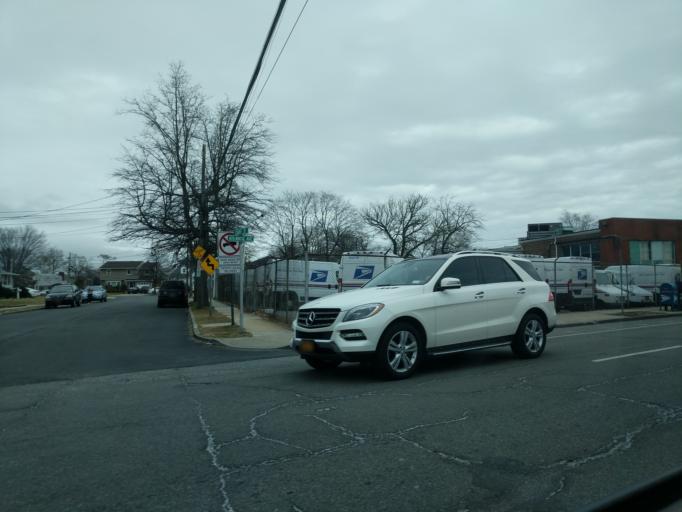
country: US
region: New York
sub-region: Nassau County
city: Oceanside
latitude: 40.6395
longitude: -73.6439
